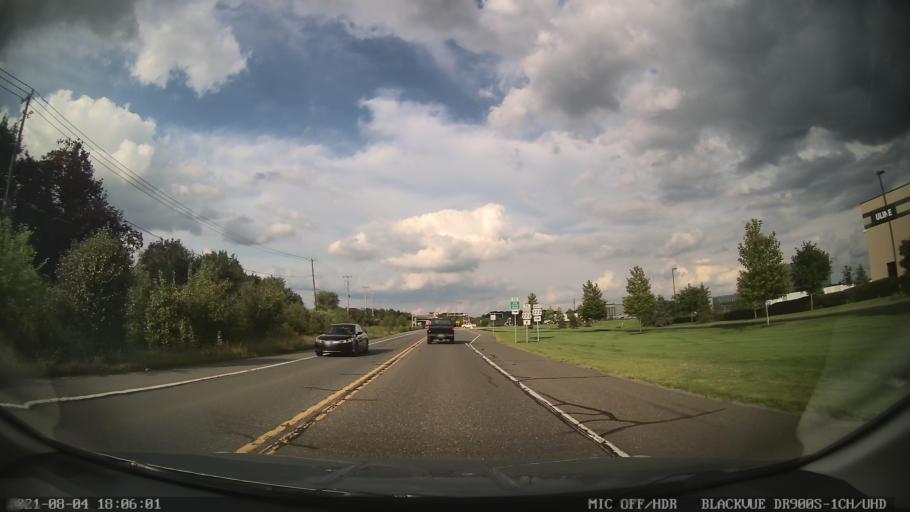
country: US
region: Pennsylvania
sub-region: Lehigh County
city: Ancient Oaks
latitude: 40.5631
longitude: -75.5894
